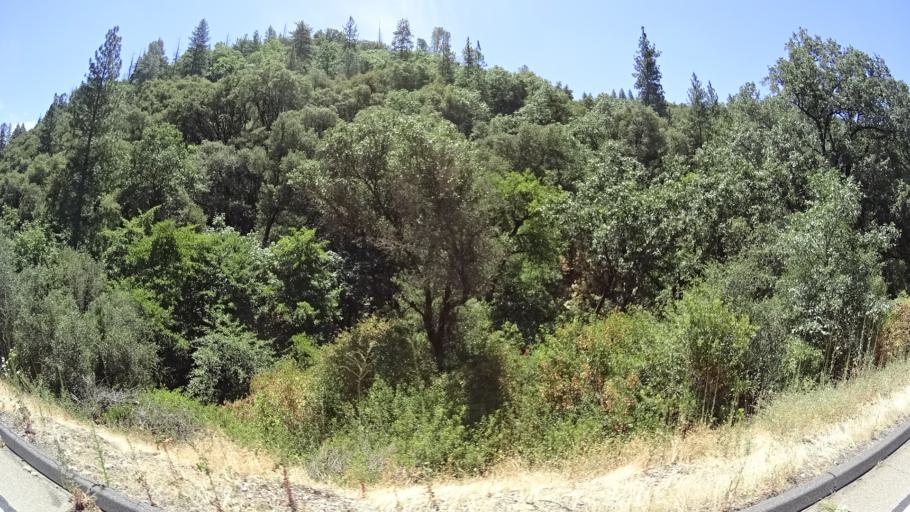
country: US
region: California
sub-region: Calaveras County
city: Murphys
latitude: 38.1327
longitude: -120.4797
